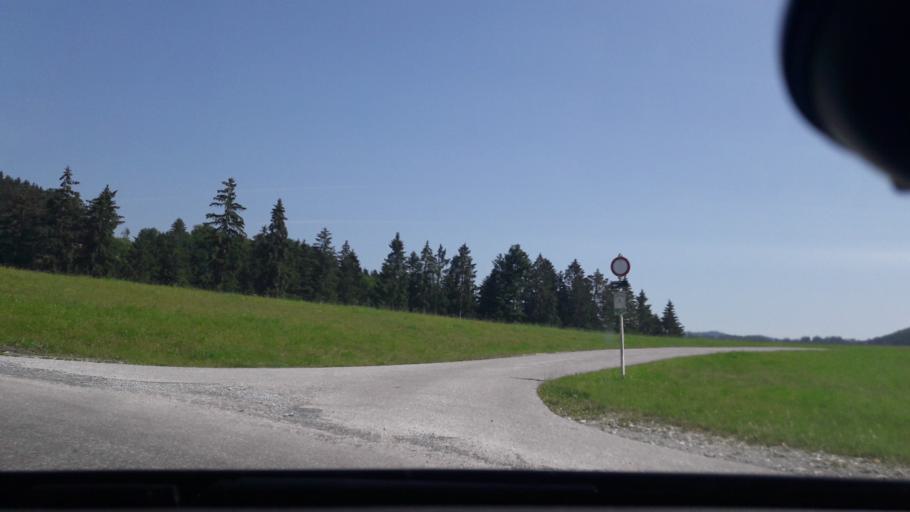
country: AT
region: Styria
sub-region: Politischer Bezirk Voitsberg
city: Sodingberg
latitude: 47.1125
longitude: 15.1602
